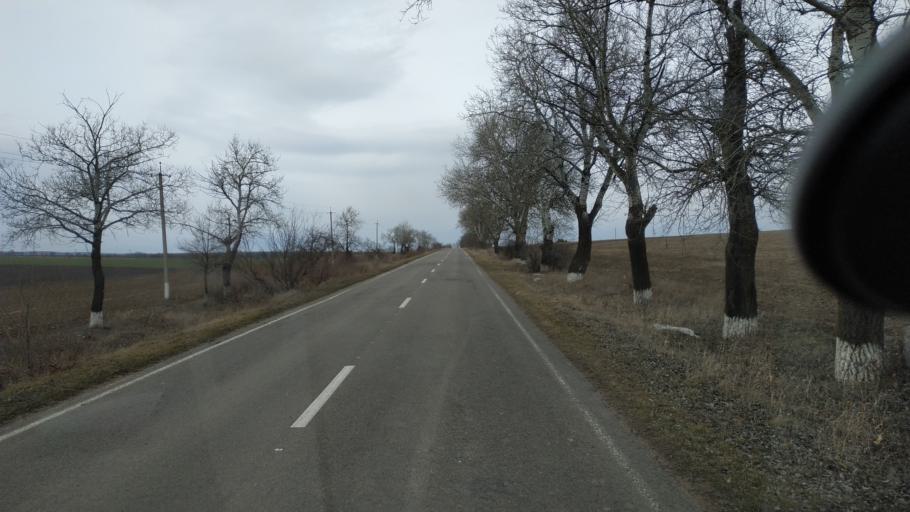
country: MD
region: Telenesti
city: Cocieri
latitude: 47.3732
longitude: 29.1108
